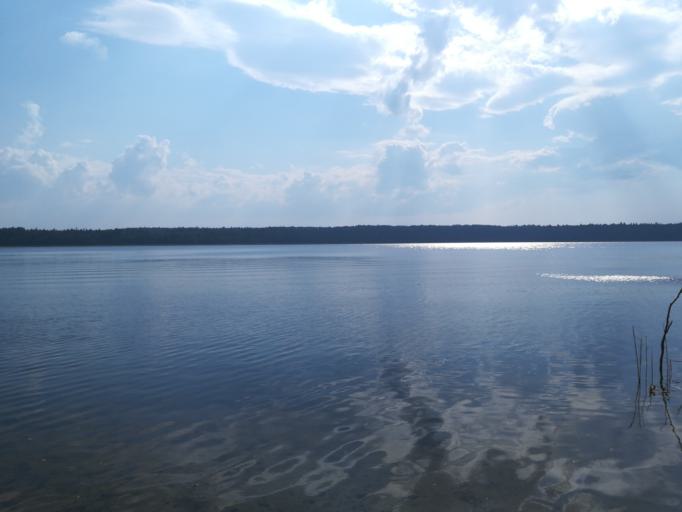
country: RU
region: Leningrad
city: Ust'-Luga
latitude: 59.7460
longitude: 28.1620
